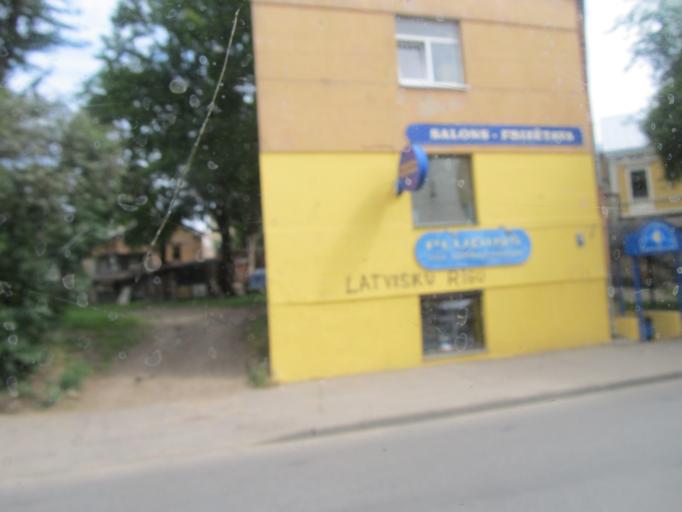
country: LV
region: Riga
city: Riga
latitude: 56.9429
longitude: 24.0789
